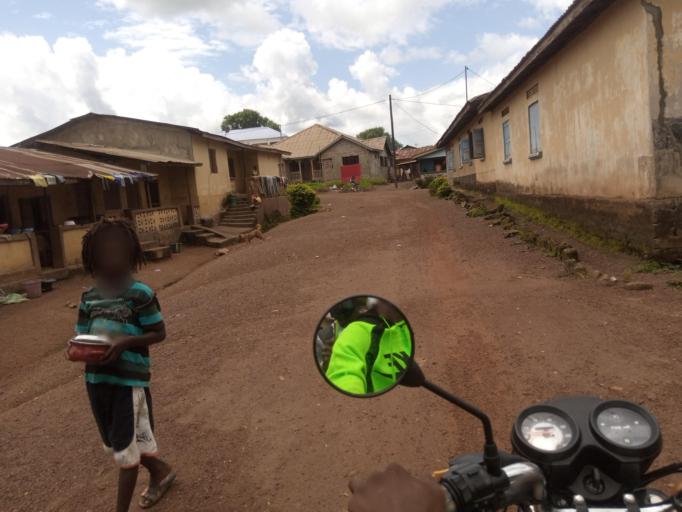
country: SL
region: Northern Province
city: Port Loko
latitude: 8.7615
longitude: -12.7823
